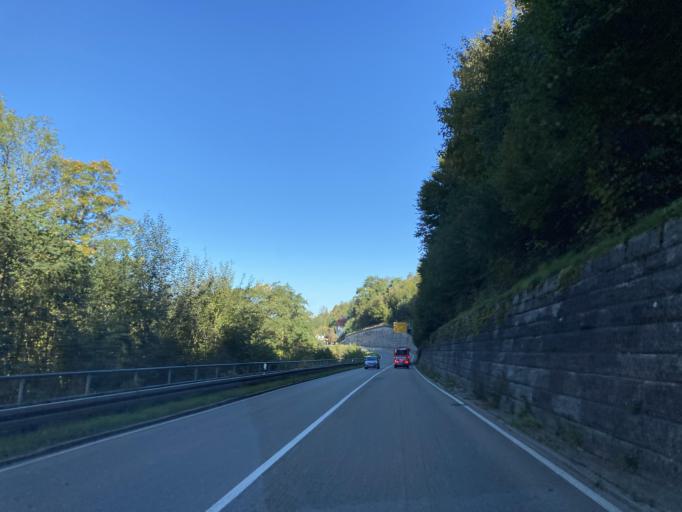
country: DE
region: Baden-Wuerttemberg
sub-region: Freiburg Region
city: Hornberg
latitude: 48.2033
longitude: 8.2346
